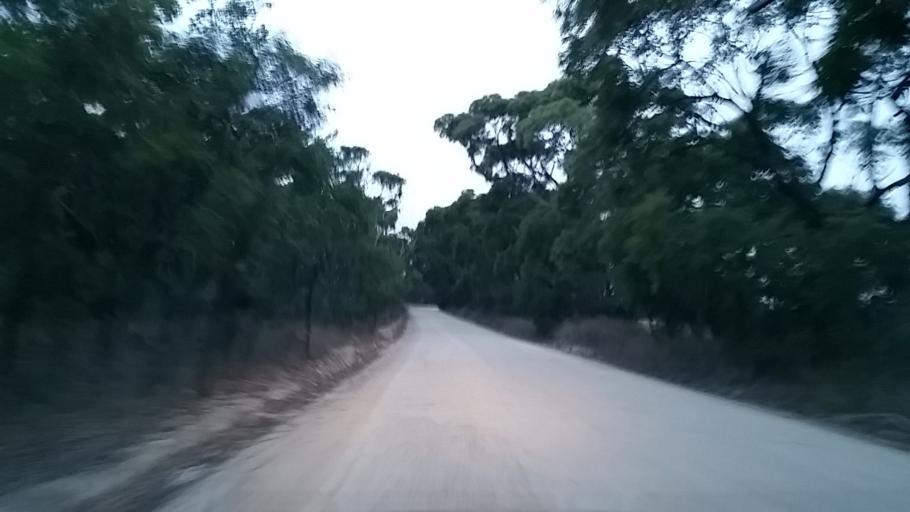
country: AU
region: South Australia
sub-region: Yankalilla
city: Normanville
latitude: -35.6113
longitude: 138.1640
